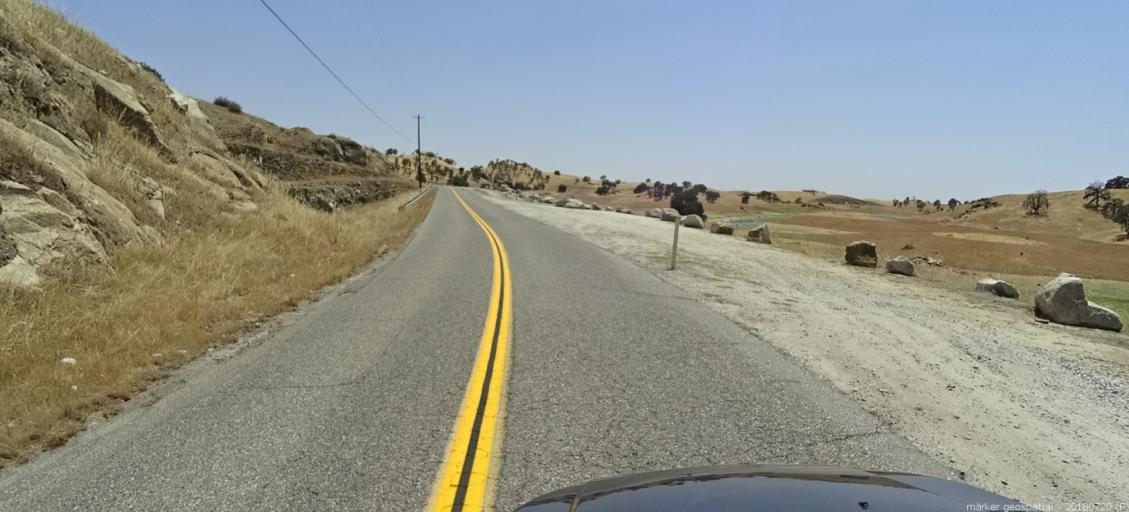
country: US
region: California
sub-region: Madera County
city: Yosemite Lakes
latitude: 37.1116
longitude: -119.8678
